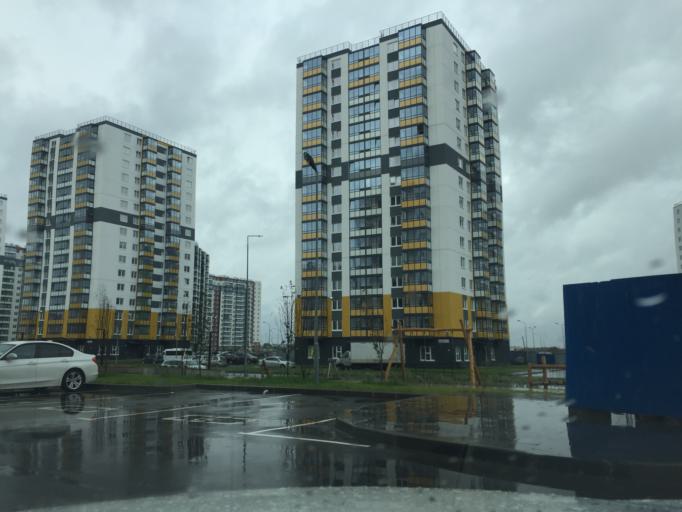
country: RU
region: St.-Petersburg
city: Sosnovaya Polyana
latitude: 59.7904
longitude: 30.1665
